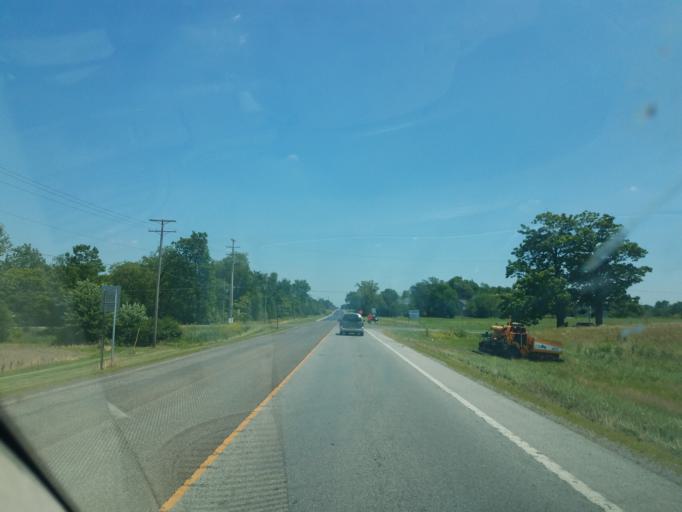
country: US
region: Ohio
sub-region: Allen County
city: Lima
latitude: 40.7312
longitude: -83.9951
